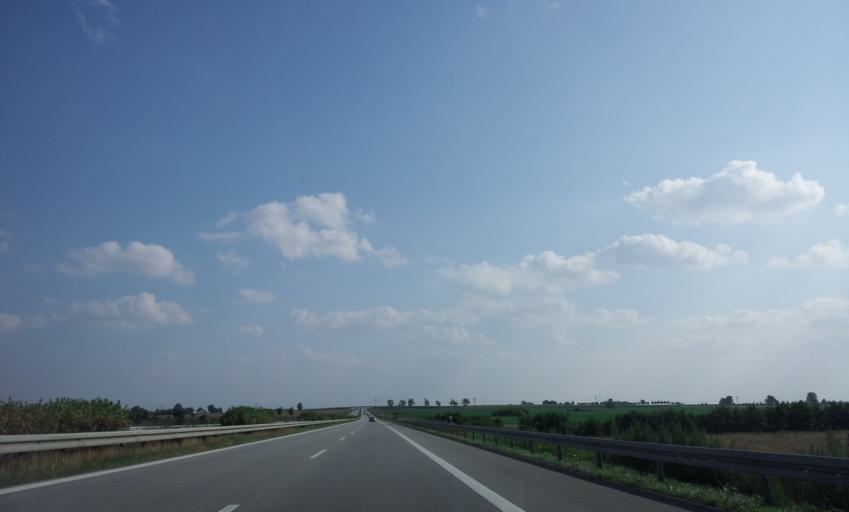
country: DE
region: Mecklenburg-Vorpommern
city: Burow
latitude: 53.8351
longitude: 13.3272
